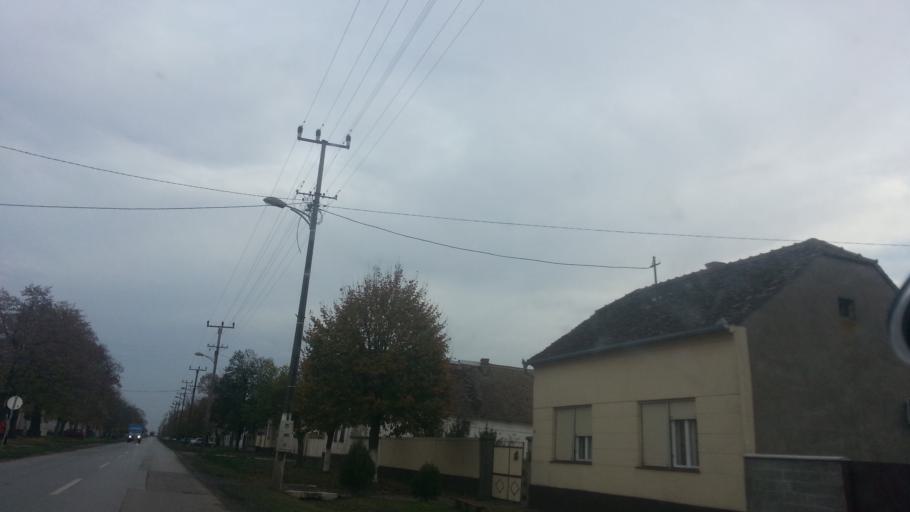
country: RS
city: Golubinci
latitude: 44.9831
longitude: 20.0709
